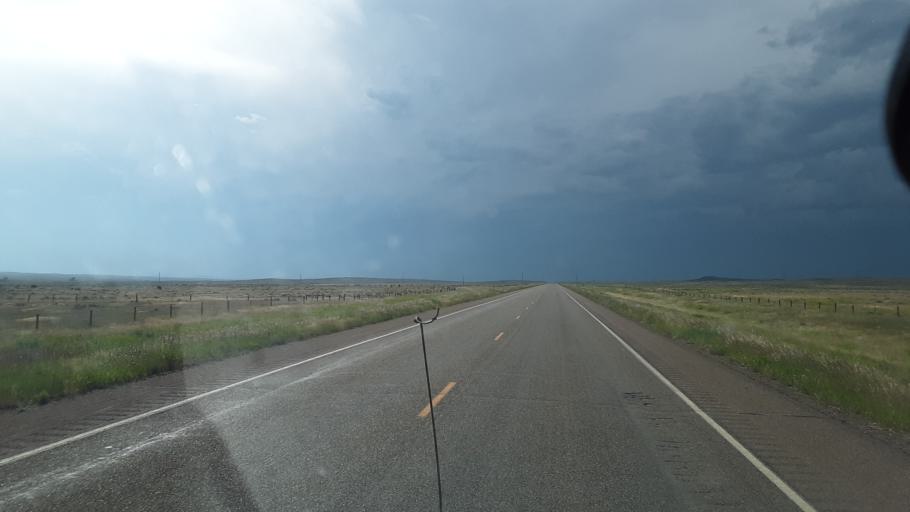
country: US
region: Montana
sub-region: Carter County
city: Ekalaka
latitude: 45.1360
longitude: -104.6837
